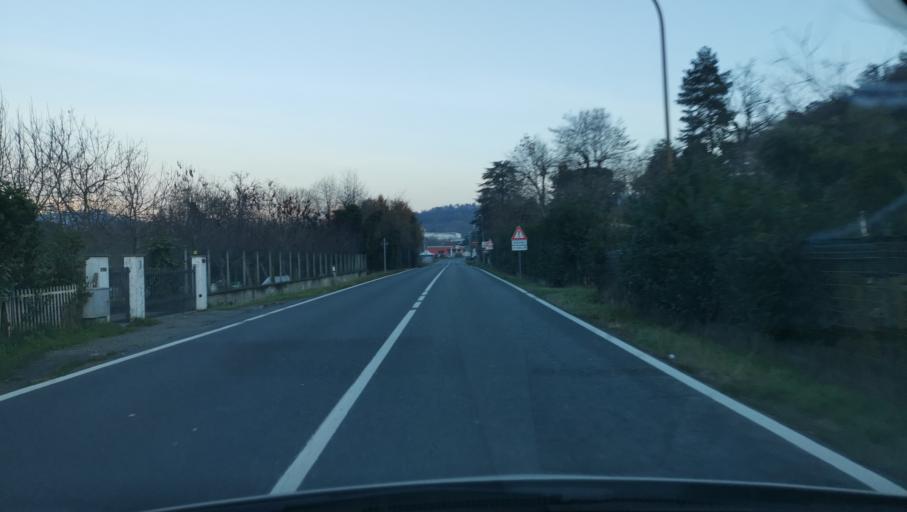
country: IT
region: Piedmont
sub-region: Provincia di Torino
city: Barone Canavese
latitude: 45.3180
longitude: 7.8788
